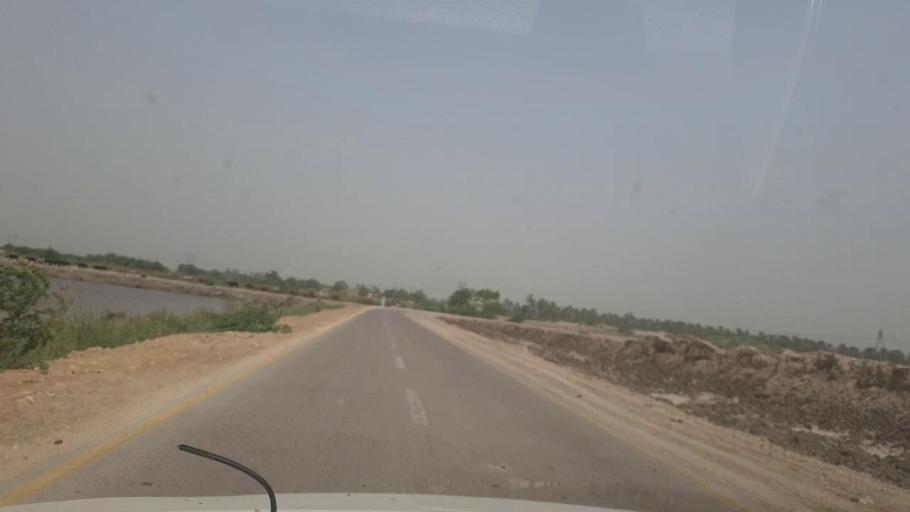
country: PK
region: Sindh
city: Kot Diji
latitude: 27.4028
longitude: 68.6585
